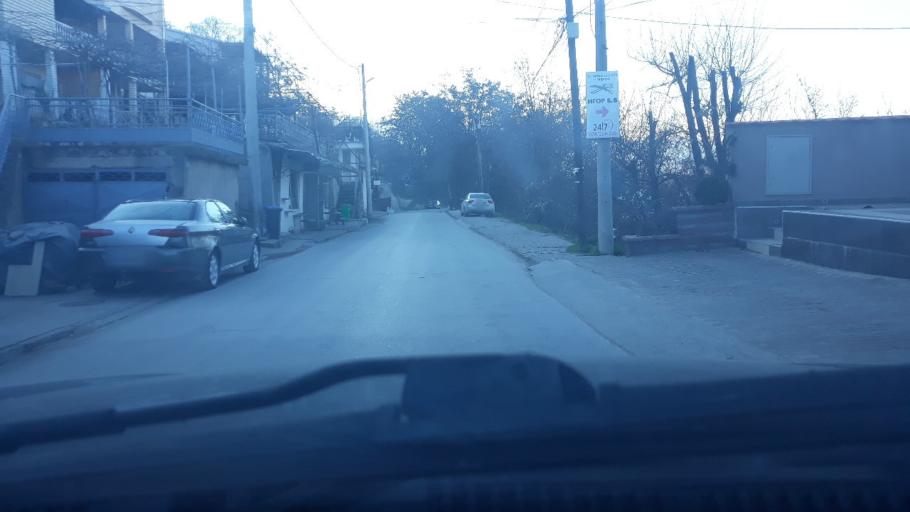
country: MK
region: Strumica
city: Strumica
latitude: 41.4386
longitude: 22.6284
